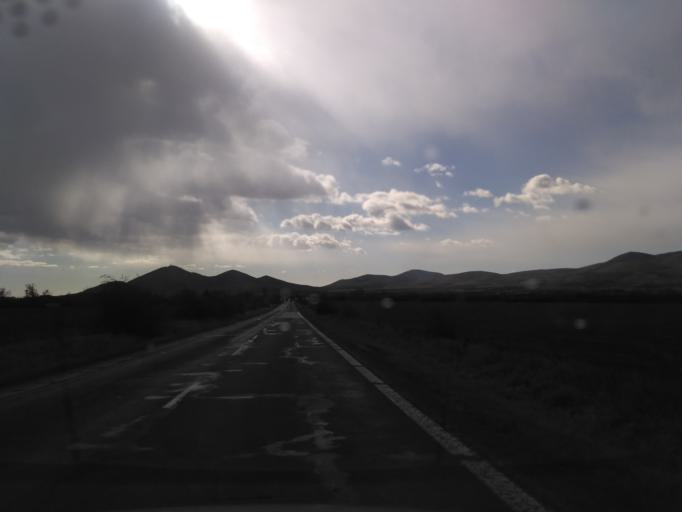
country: HU
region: Borsod-Abauj-Zemplen
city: Satoraljaujhely
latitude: 48.4741
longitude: 21.6413
